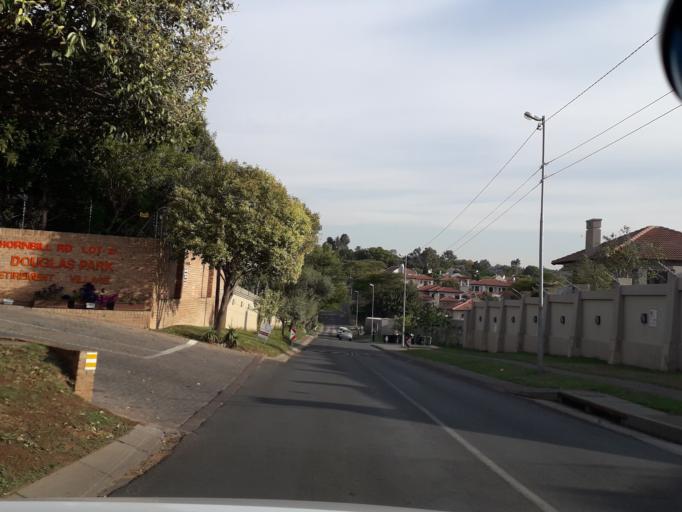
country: ZA
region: Gauteng
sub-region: City of Johannesburg Metropolitan Municipality
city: Diepsloot
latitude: -26.0479
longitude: 27.9902
